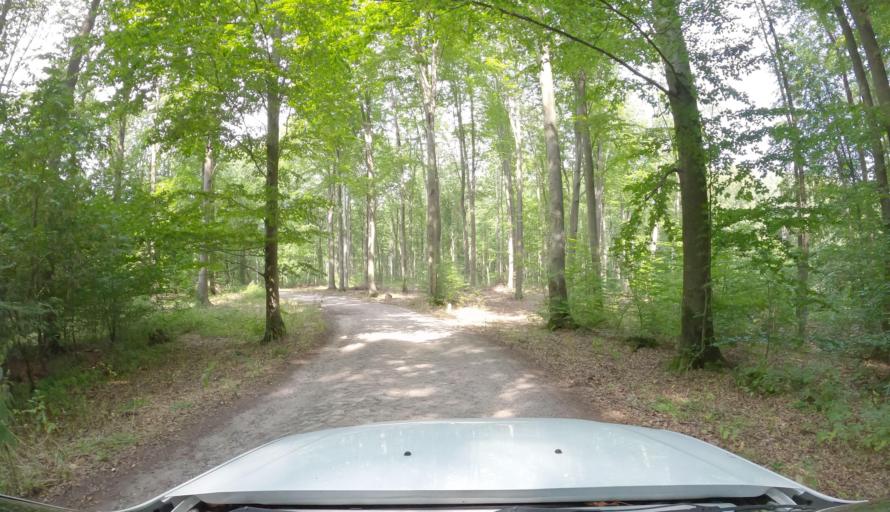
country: PL
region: West Pomeranian Voivodeship
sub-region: Powiat drawski
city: Czaplinek
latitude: 53.5816
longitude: 16.2681
